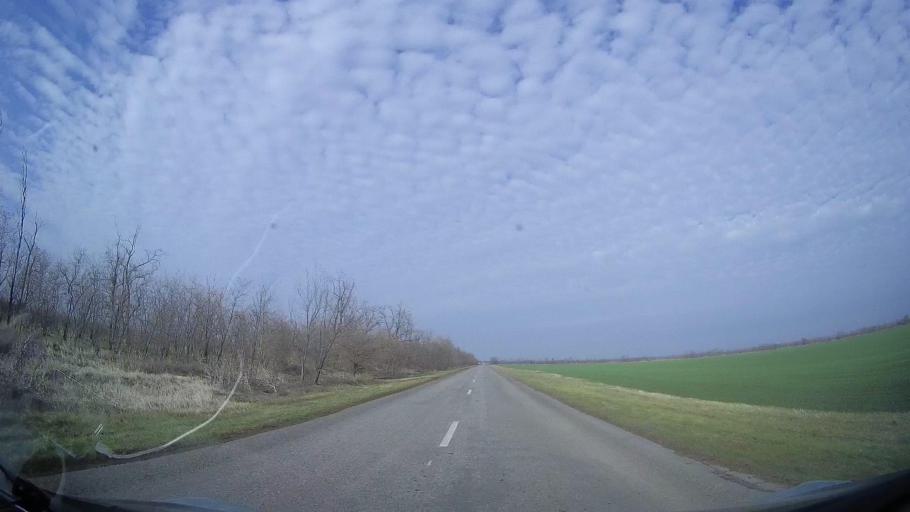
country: RU
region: Rostov
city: Gigant
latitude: 46.8710
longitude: 41.2746
